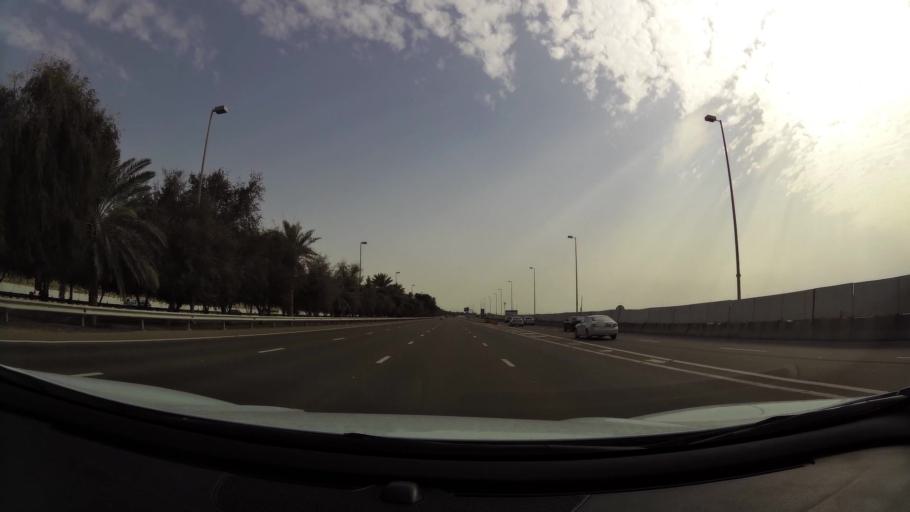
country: AE
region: Abu Dhabi
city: Abu Dhabi
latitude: 24.4285
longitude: 54.6775
